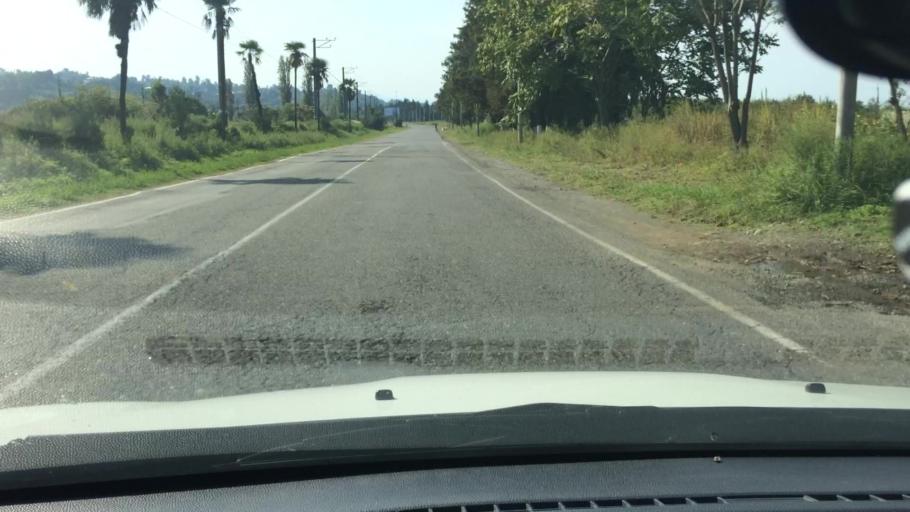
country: GE
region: Ajaria
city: Kobuleti
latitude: 41.7940
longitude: 41.7704
